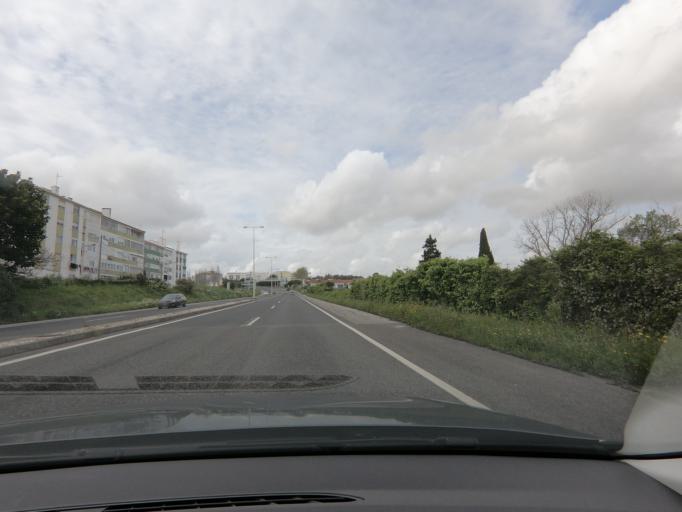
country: PT
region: Lisbon
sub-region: Cascais
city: Sao Domingos de Rana
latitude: 38.7011
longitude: -9.3335
